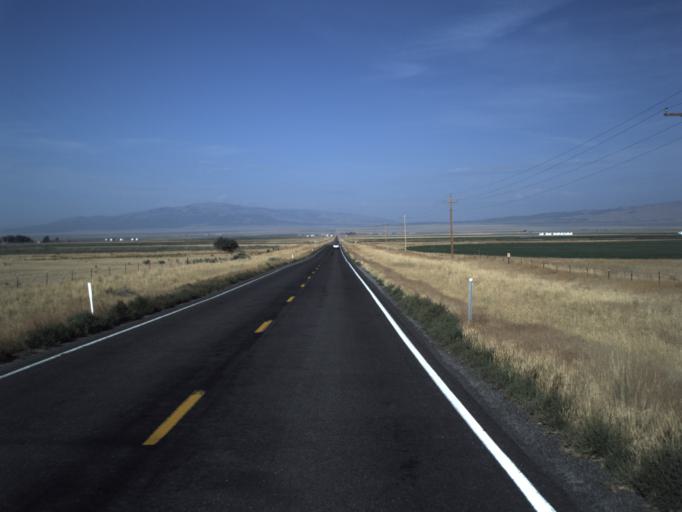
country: US
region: Idaho
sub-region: Oneida County
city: Malad City
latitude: 41.9674
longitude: -112.8155
